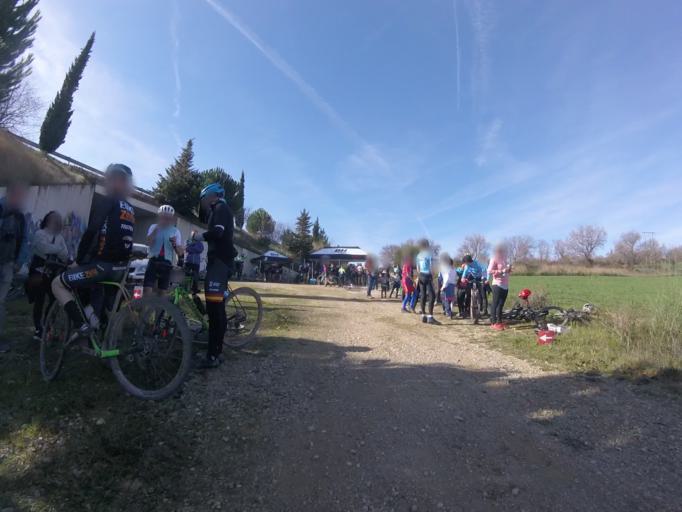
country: ES
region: Navarre
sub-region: Provincia de Navarra
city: Villatuerta
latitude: 42.6682
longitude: -1.9596
